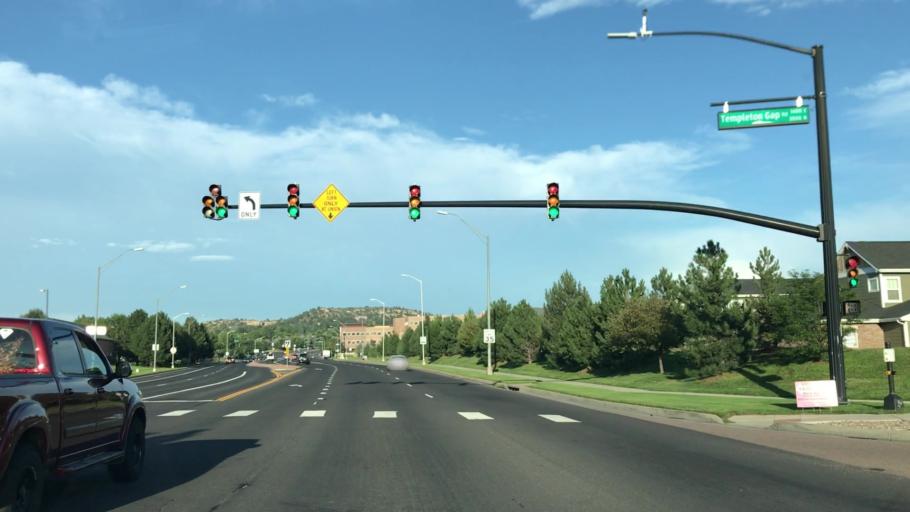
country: US
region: Colorado
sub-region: El Paso County
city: Colorado Springs
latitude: 38.8735
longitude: -104.7996
